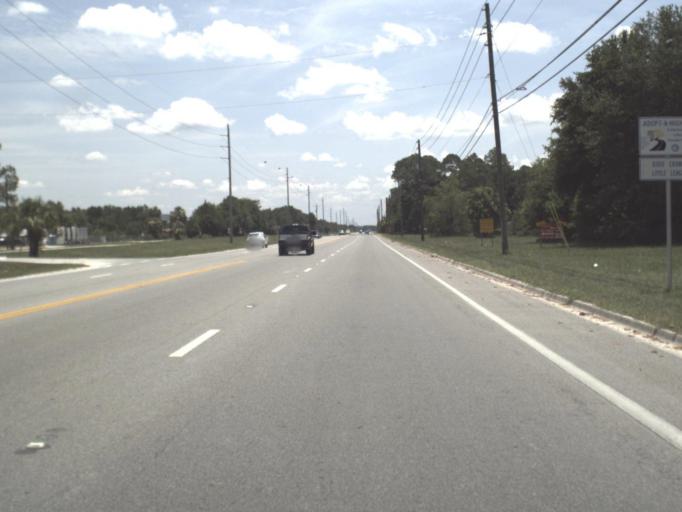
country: US
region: Florida
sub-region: Dixie County
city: Cross City
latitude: 29.6296
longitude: -83.1168
